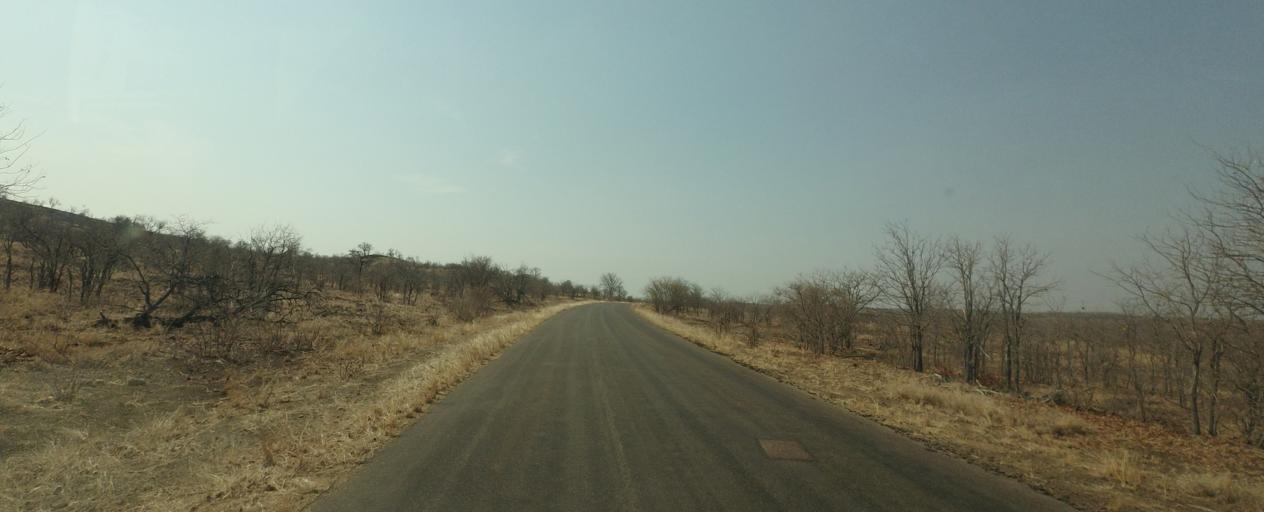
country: ZA
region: Limpopo
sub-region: Mopani District Municipality
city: Phalaborwa
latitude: -23.9900
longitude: 31.6421
